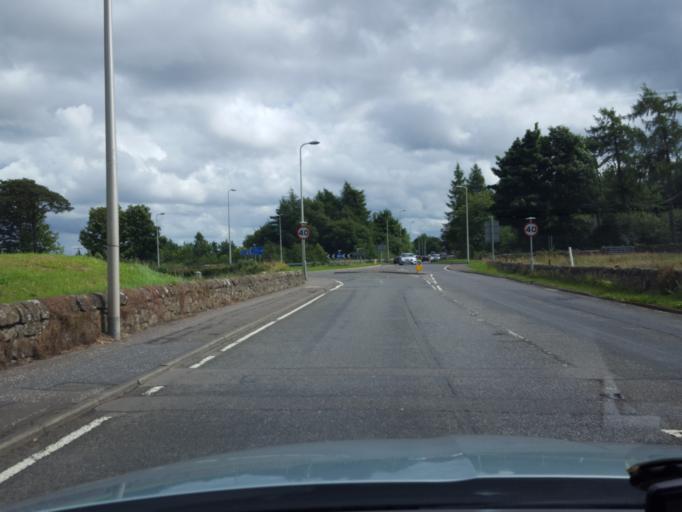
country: GB
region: Scotland
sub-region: Falkirk
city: Larbert
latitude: 56.0337
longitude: -3.8521
